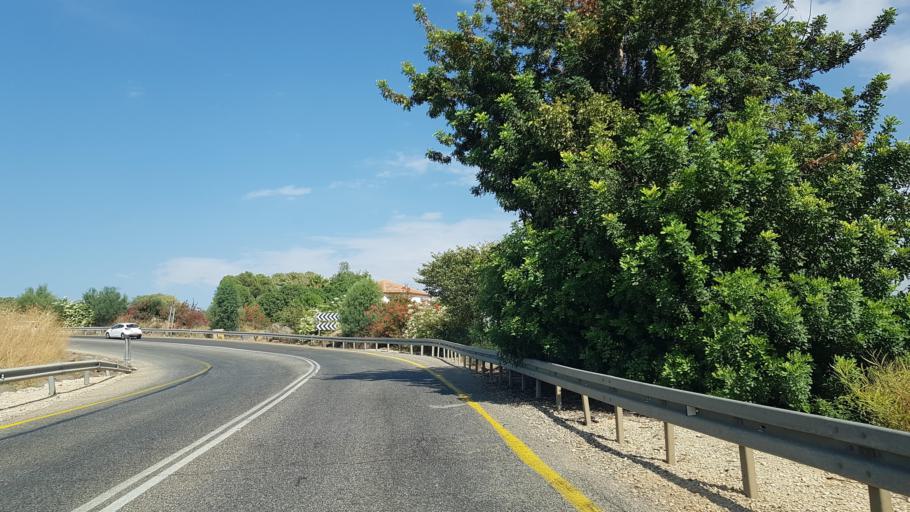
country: IL
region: Northern District
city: Rosh Pinna
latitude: 32.9059
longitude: 35.5496
